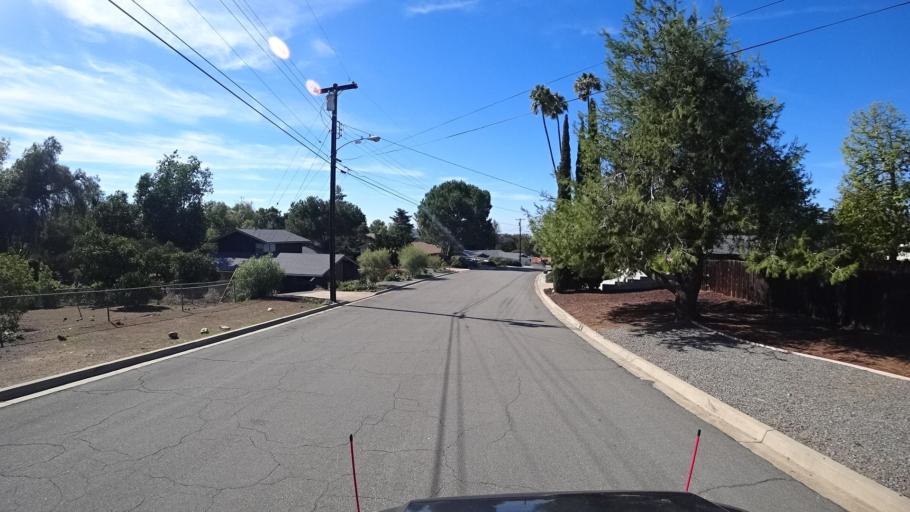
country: US
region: California
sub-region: San Diego County
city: Casa de Oro-Mount Helix
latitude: 32.7569
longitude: -116.9559
